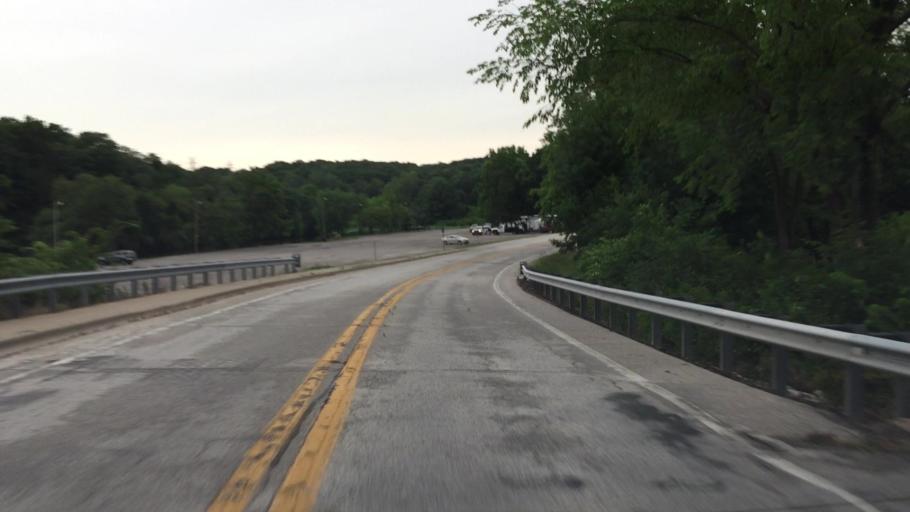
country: US
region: Illinois
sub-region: Hancock County
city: Hamilton
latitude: 40.4039
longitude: -91.3520
